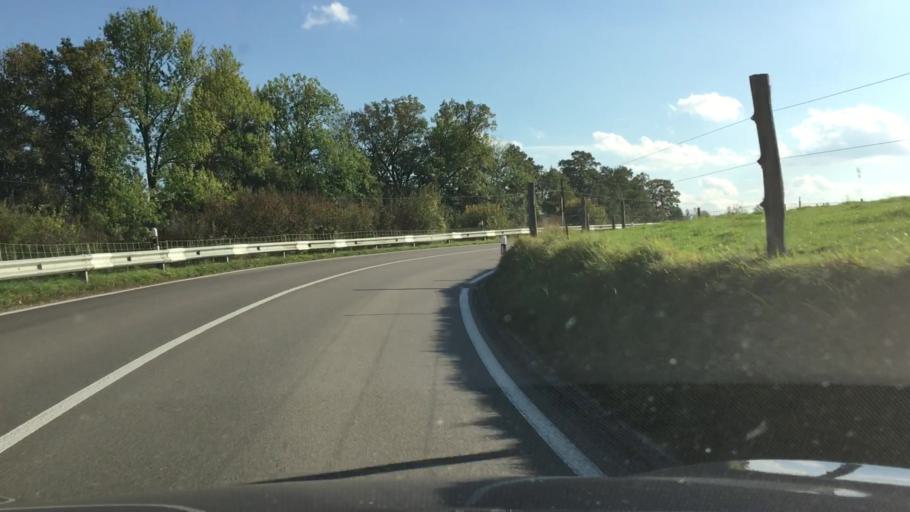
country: CH
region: Saint Gallen
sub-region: Wahlkreis St. Gallen
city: Waldkirch
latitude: 47.4708
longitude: 9.2518
